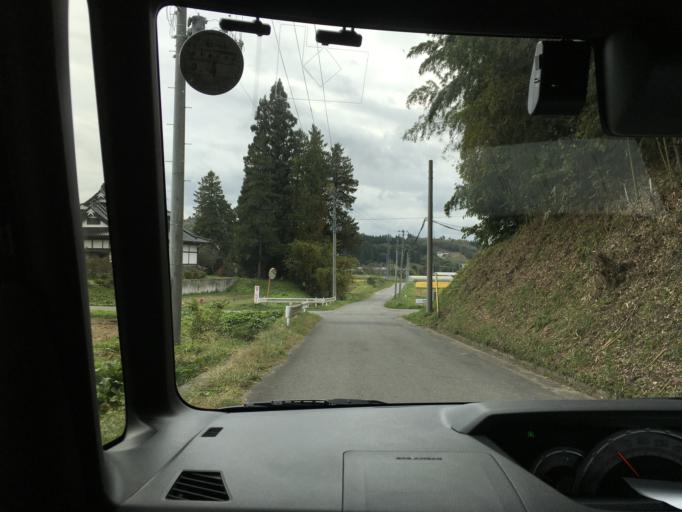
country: JP
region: Iwate
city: Ichinoseki
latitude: 39.0204
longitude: 141.3501
